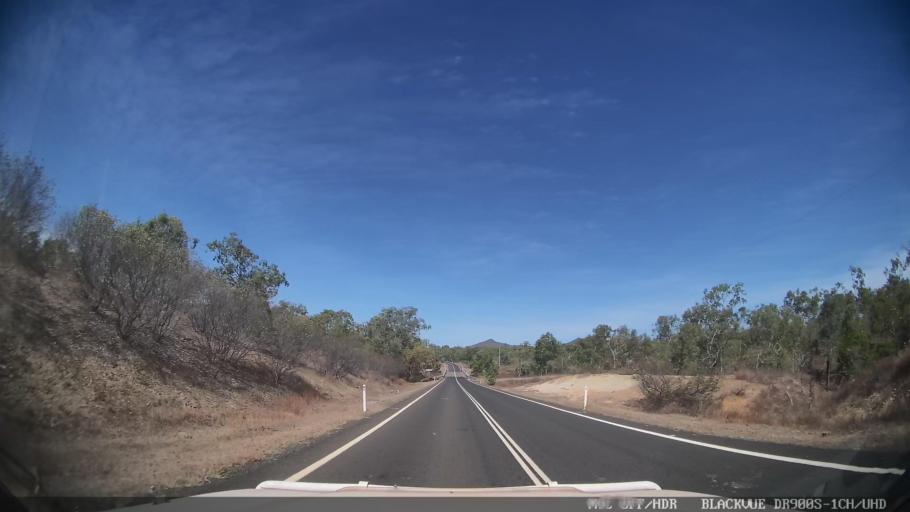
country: AU
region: Queensland
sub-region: Cook
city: Cooktown
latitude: -15.7100
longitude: 144.6131
